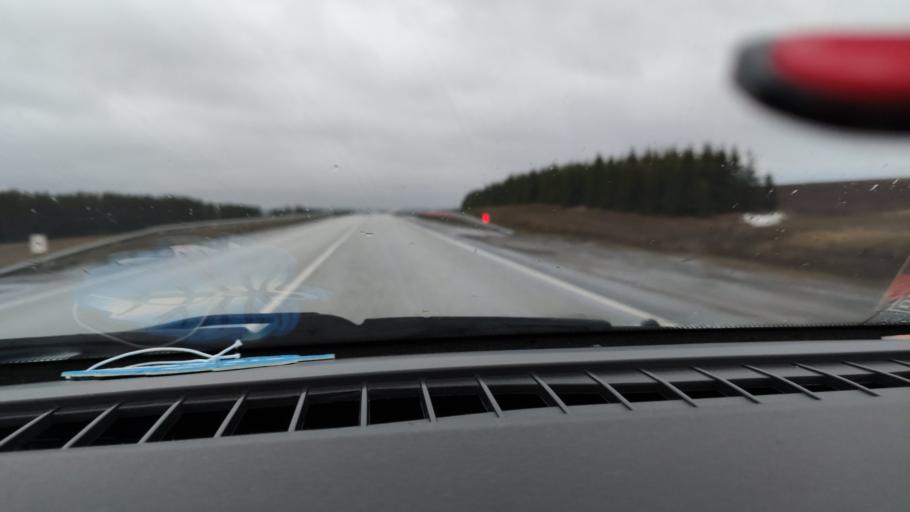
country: RU
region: Tatarstan
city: Mendeleyevsk
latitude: 56.0418
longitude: 52.3884
